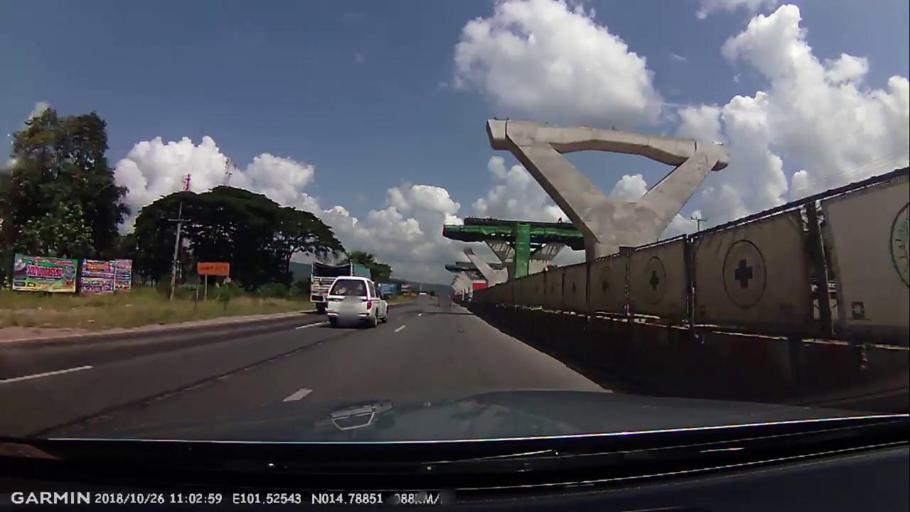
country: TH
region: Nakhon Ratchasima
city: Pak Chong
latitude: 14.7888
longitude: 101.5255
